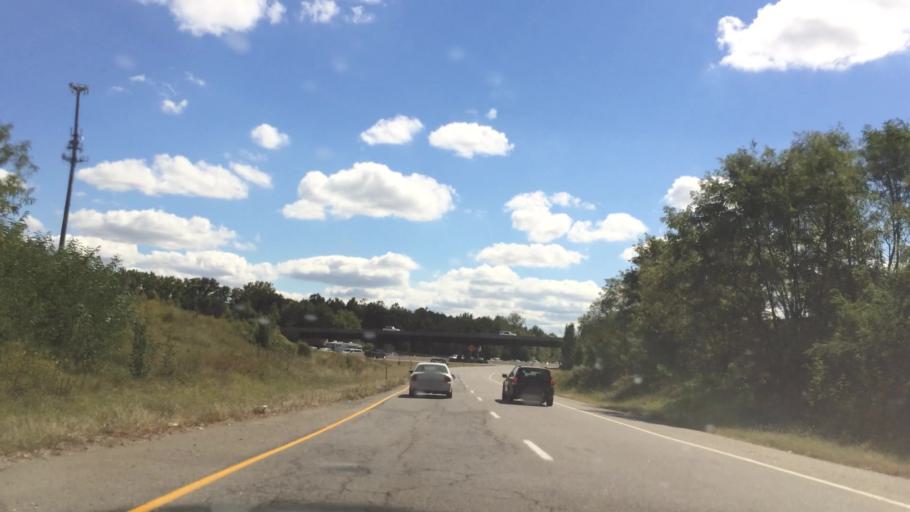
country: US
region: Virginia
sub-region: Henrico County
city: Glen Allen
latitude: 37.6855
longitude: -77.4535
